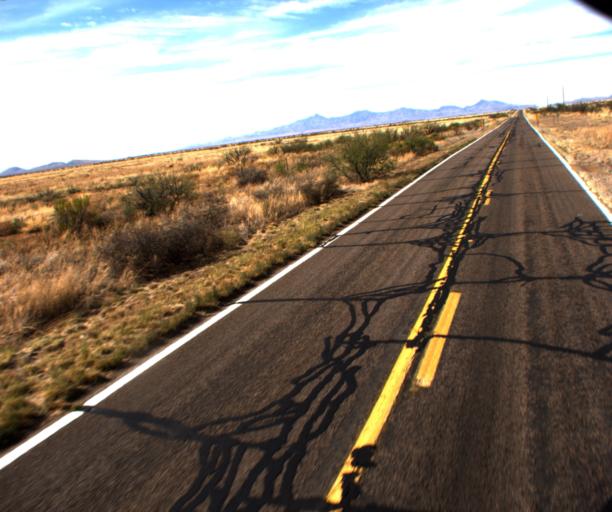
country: US
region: Arizona
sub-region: Cochise County
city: Willcox
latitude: 31.9133
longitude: -109.4914
